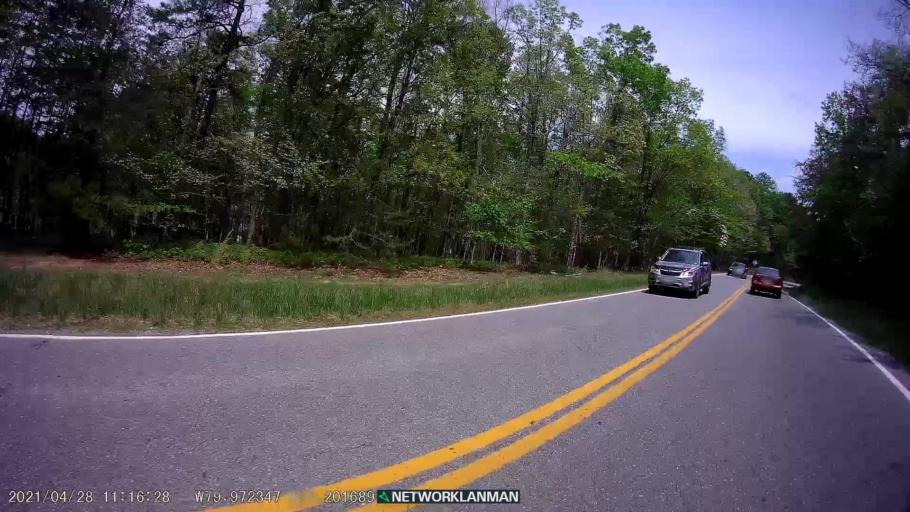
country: US
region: Virginia
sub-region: Roanoke County
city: Narrows
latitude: 37.2019
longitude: -79.9719
